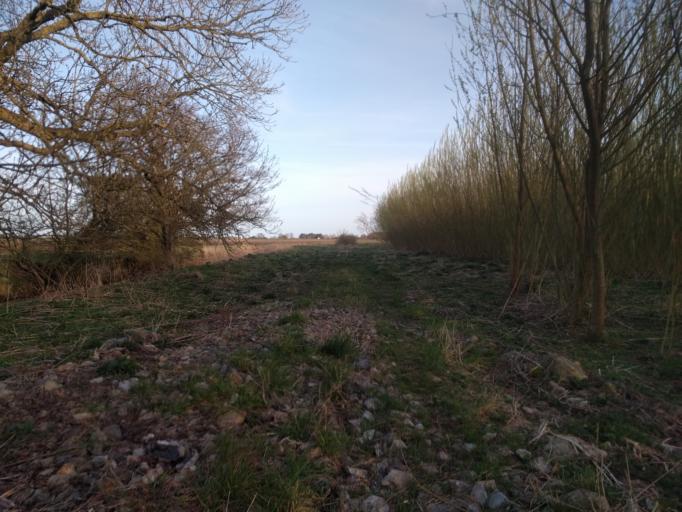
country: DK
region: South Denmark
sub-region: Kerteminde Kommune
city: Munkebo
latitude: 55.4117
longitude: 10.5509
